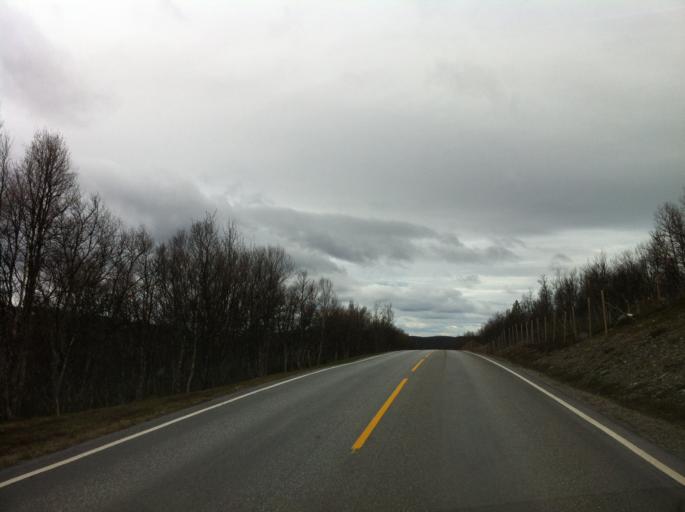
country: NO
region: Sor-Trondelag
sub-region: Tydal
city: Aas
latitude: 62.6365
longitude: 11.9485
